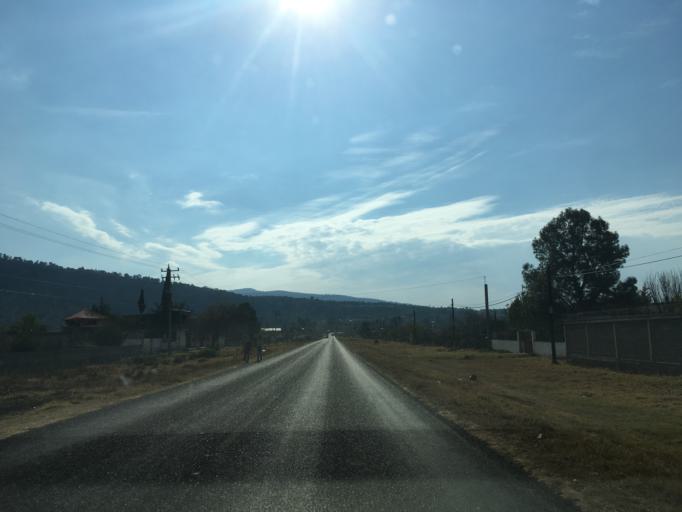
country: MX
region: Michoacan
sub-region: Patzcuaro
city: Santa Ana Chapitiro
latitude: 19.5334
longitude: -101.6415
